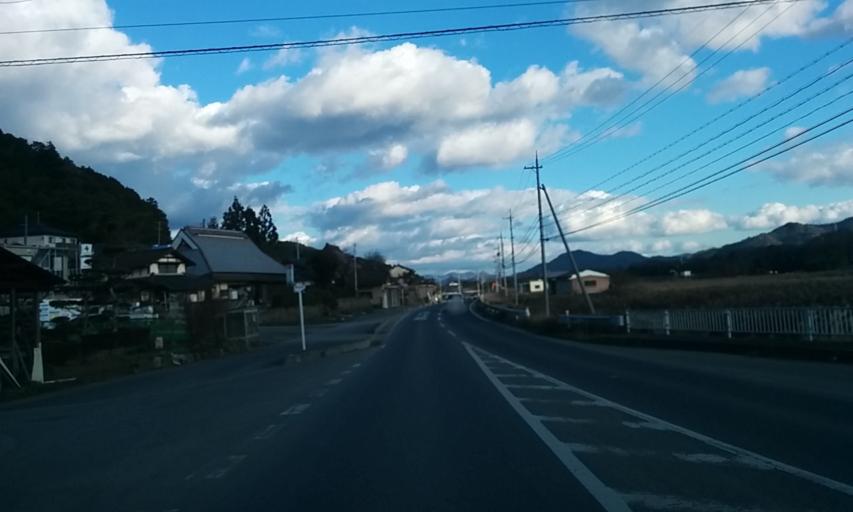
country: JP
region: Kyoto
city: Fukuchiyama
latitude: 35.3124
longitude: 135.1588
